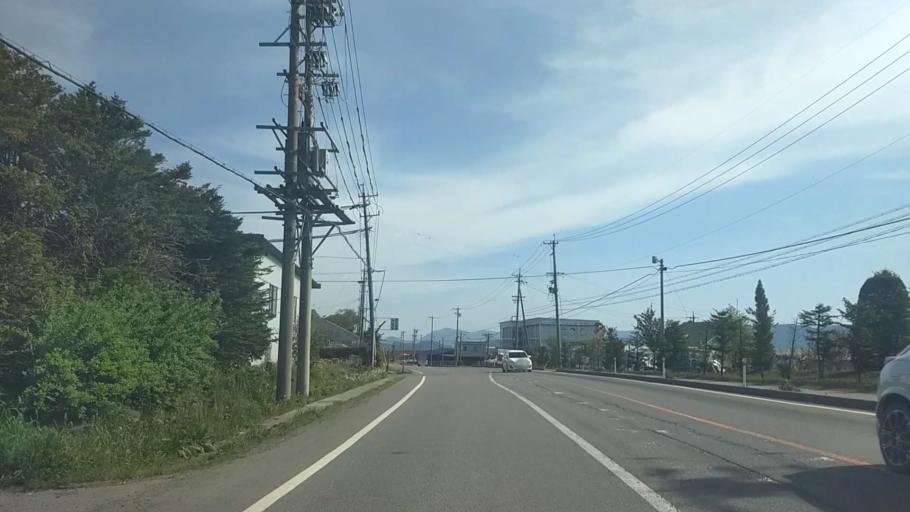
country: JP
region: Nagano
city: Saku
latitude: 35.9804
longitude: 138.4837
